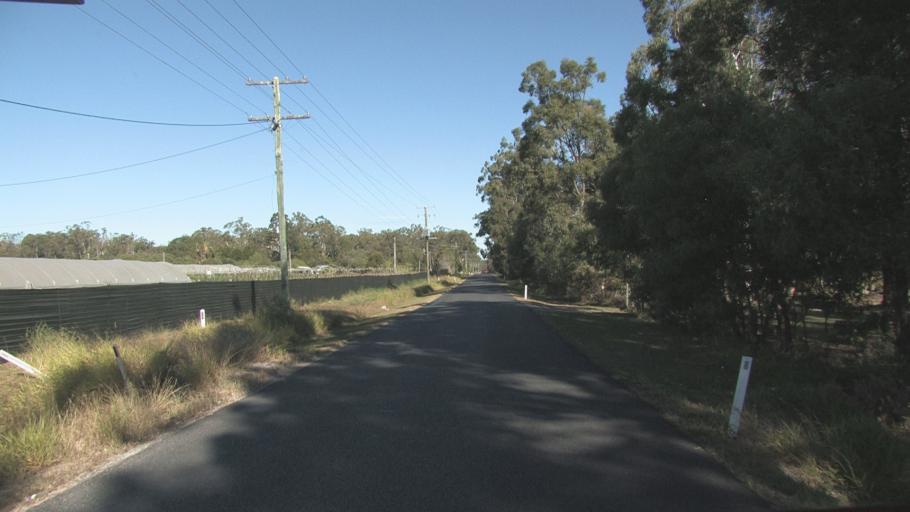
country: AU
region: Queensland
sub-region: Logan
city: Logan Reserve
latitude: -27.7245
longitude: 153.0733
